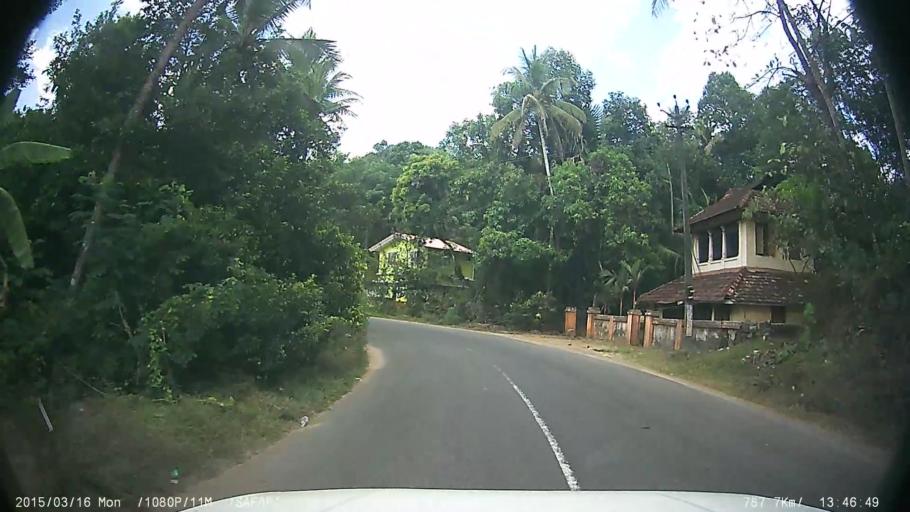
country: IN
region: Kerala
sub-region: Ernakulam
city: Muvattupuzha
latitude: 9.9171
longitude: 76.5826
